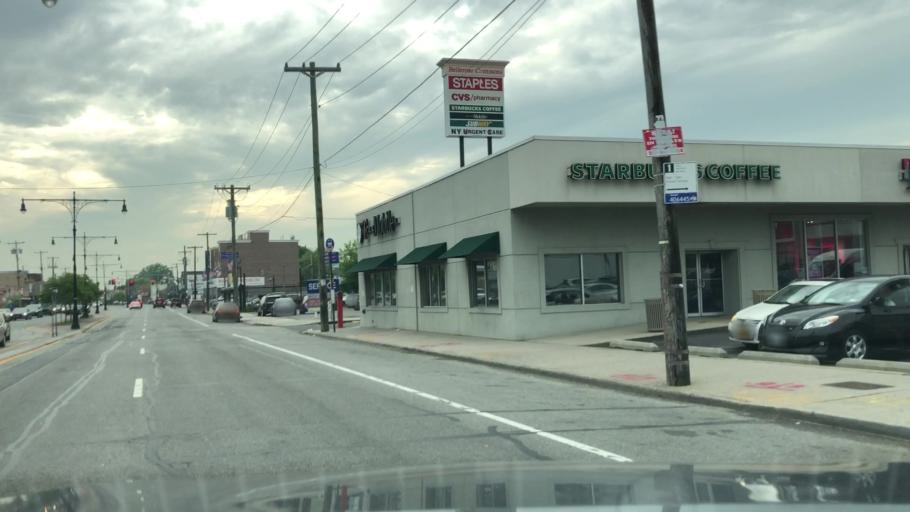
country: US
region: New York
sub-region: Nassau County
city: Bellerose
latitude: 40.7269
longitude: -73.7136
